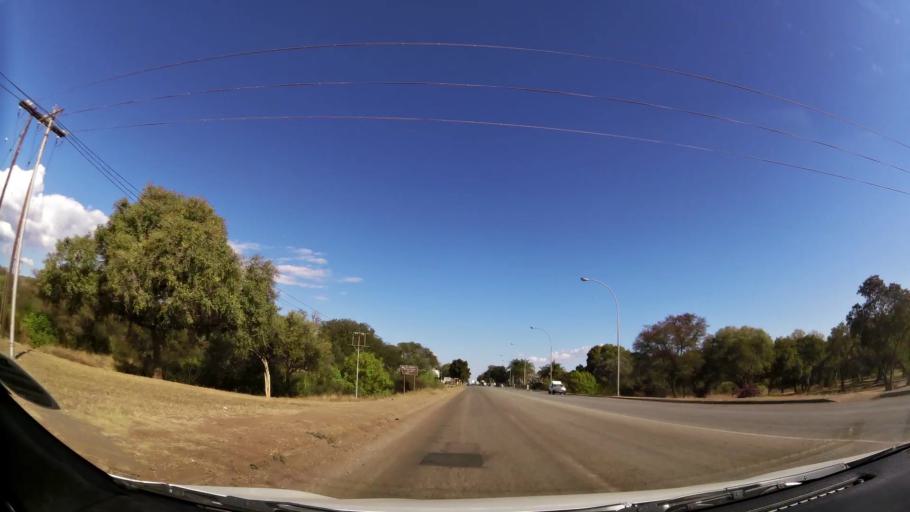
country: ZA
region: Limpopo
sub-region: Waterberg District Municipality
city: Mokopane
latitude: -24.1733
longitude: 29.0167
